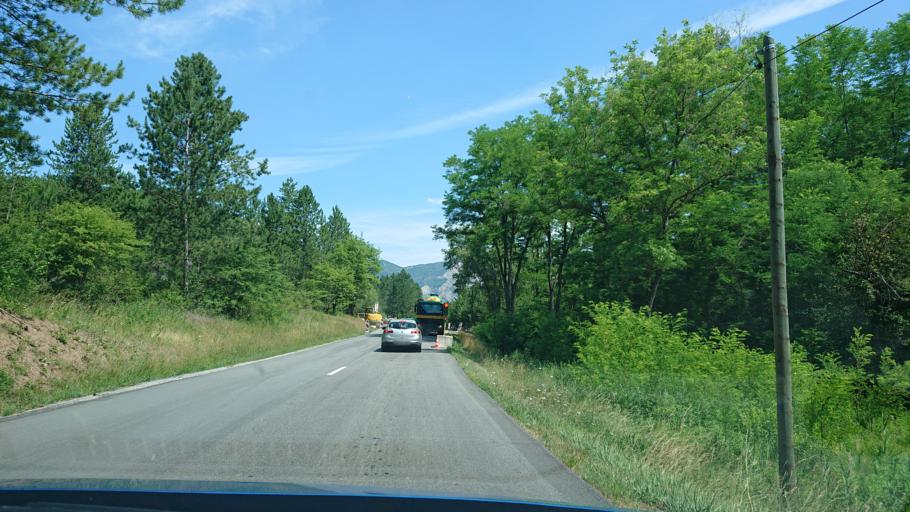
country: FR
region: Provence-Alpes-Cote d'Azur
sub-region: Departement des Hautes-Alpes
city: Tallard
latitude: 44.3202
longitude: 6.0301
